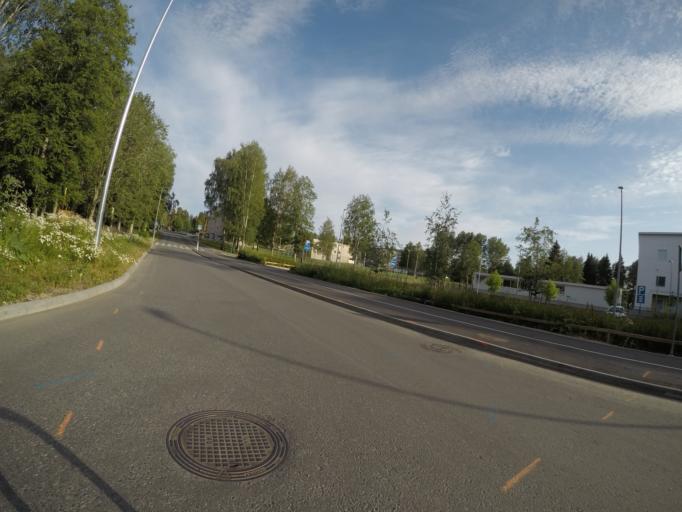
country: FI
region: Haeme
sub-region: Haemeenlinna
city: Haemeenlinna
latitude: 60.9820
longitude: 24.4057
